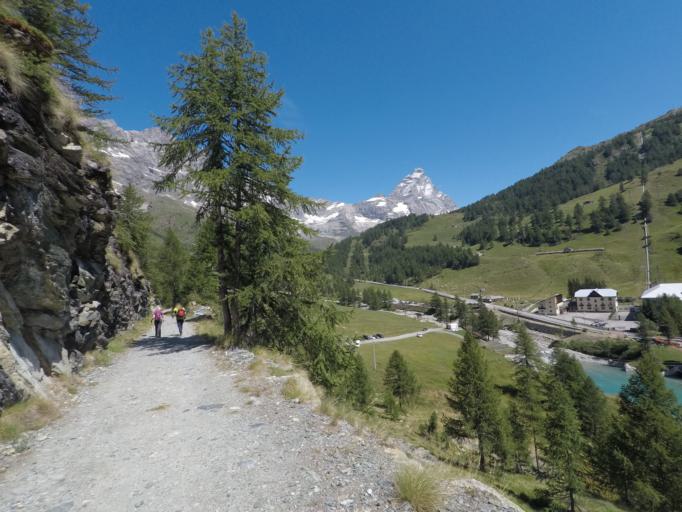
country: IT
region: Aosta Valley
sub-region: Valle d'Aosta
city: Paquier
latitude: 45.9061
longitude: 7.6138
